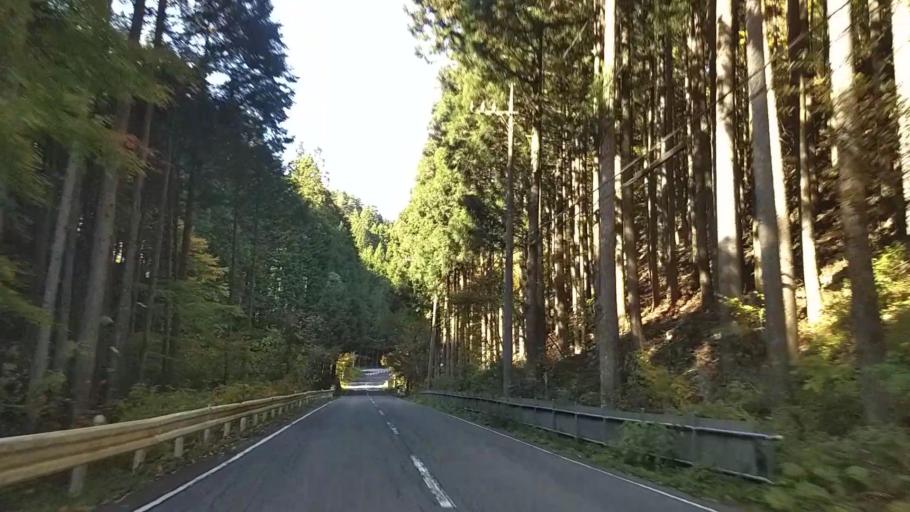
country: JP
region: Yamanashi
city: Otsuki
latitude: 35.7379
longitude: 138.9696
